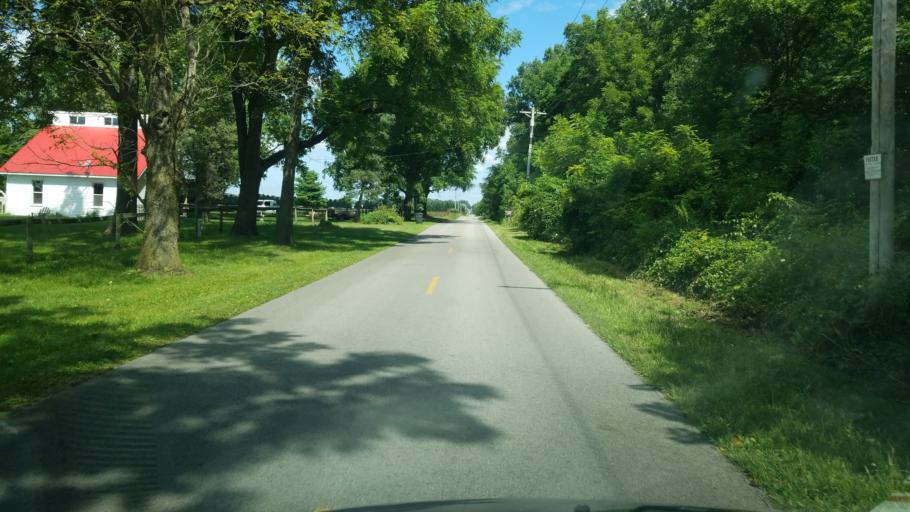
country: US
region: Ohio
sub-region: Henry County
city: Liberty Center
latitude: 41.4783
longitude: -83.9413
